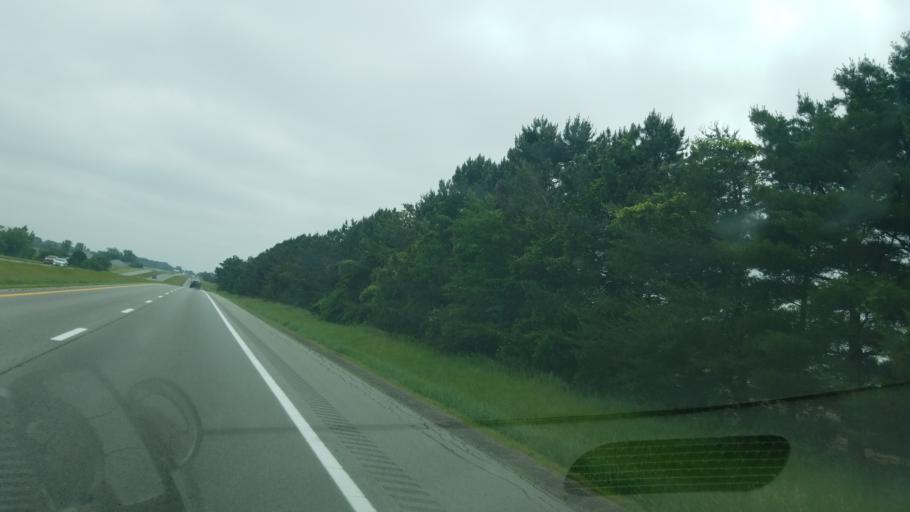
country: US
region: Ohio
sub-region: Wyandot County
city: Upper Sandusky
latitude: 40.7717
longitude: -83.2403
